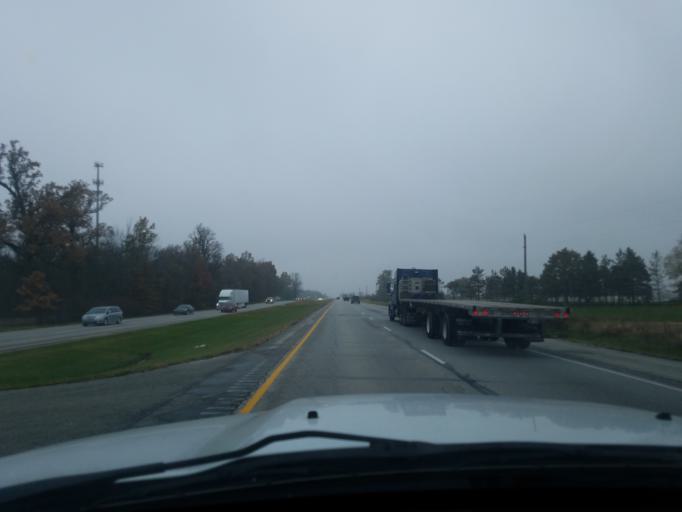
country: US
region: Indiana
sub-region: Hamilton County
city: Sheridan
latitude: 40.1506
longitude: -86.1278
